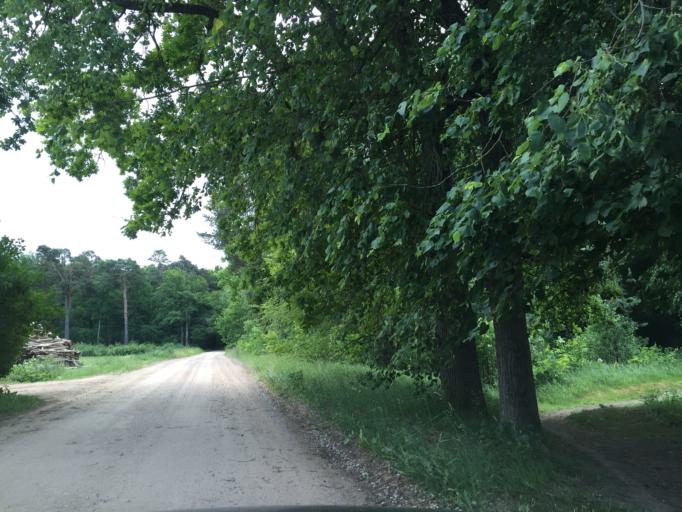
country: LV
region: Lecava
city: Iecava
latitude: 56.5884
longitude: 24.2035
